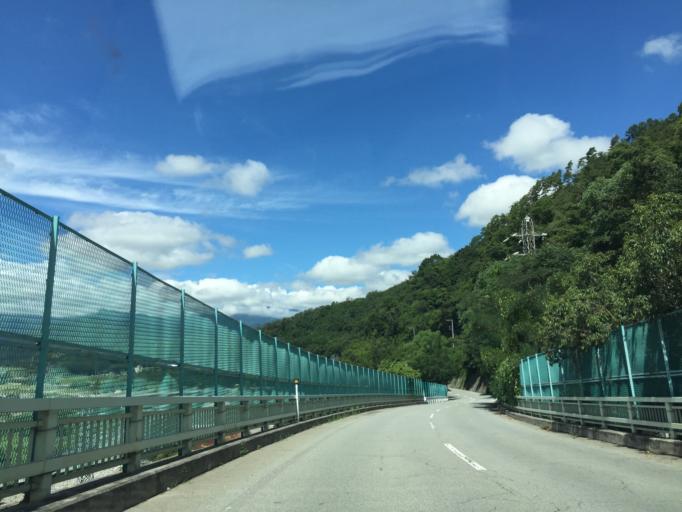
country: JP
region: Yamanashi
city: Nirasaki
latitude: 35.7869
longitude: 138.3926
